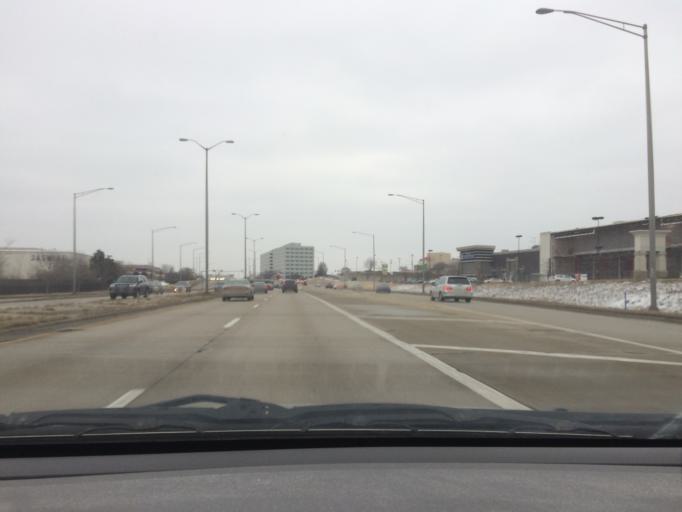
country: US
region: Illinois
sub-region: DuPage County
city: Downers Grove
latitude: 41.8346
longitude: -88.0156
